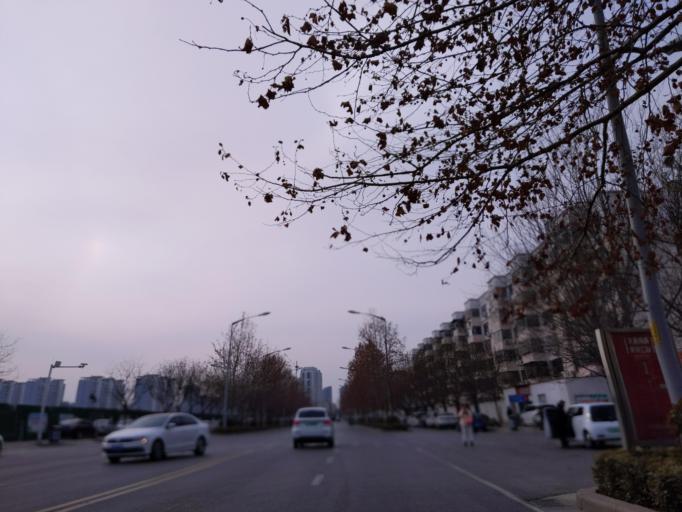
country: CN
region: Henan Sheng
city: Zhongyuanlu
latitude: 35.7583
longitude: 115.0489
